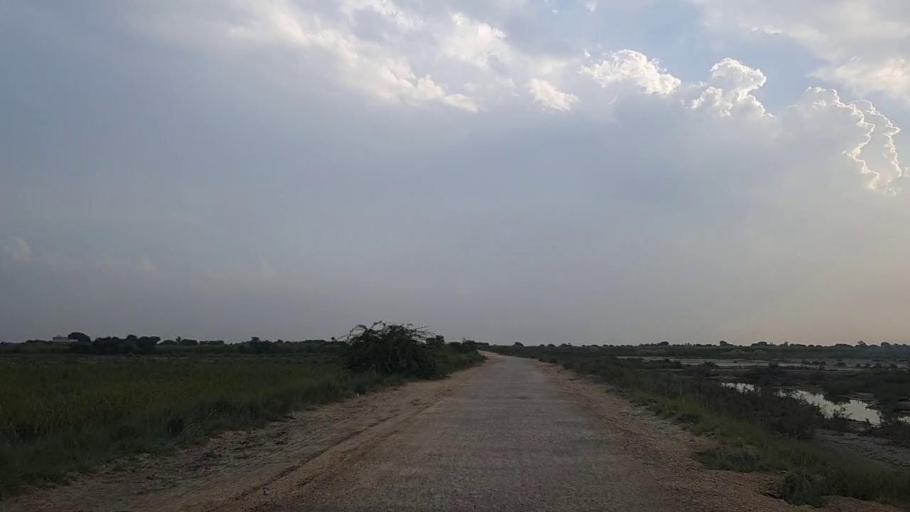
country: PK
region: Sindh
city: Daro Mehar
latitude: 24.7752
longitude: 68.1494
